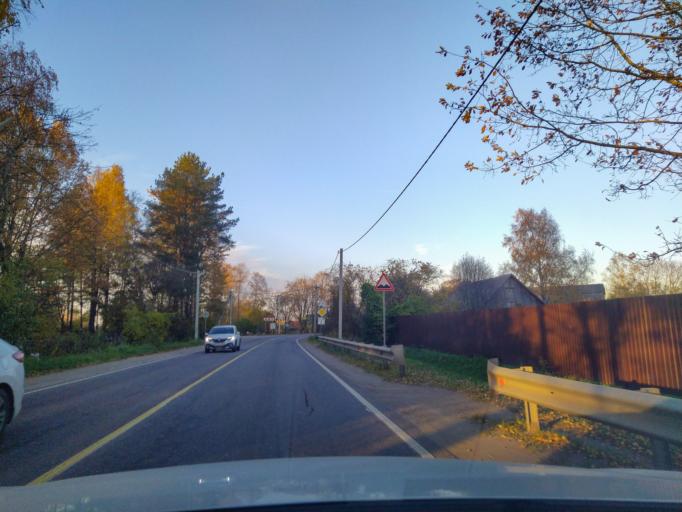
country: RU
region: Leningrad
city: Kobrinskoye
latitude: 59.4726
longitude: 30.1210
